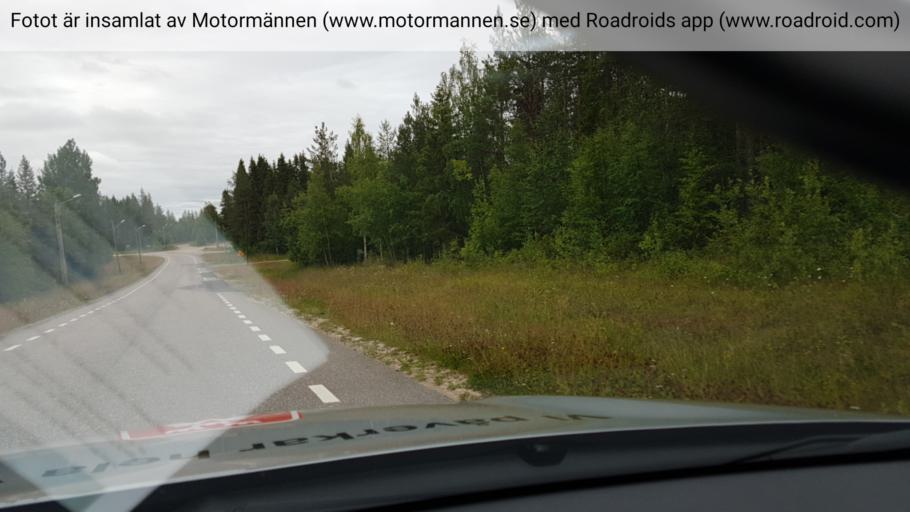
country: SE
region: Norrbotten
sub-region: Gallivare Kommun
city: Gaellivare
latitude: 67.0126
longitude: 21.8182
